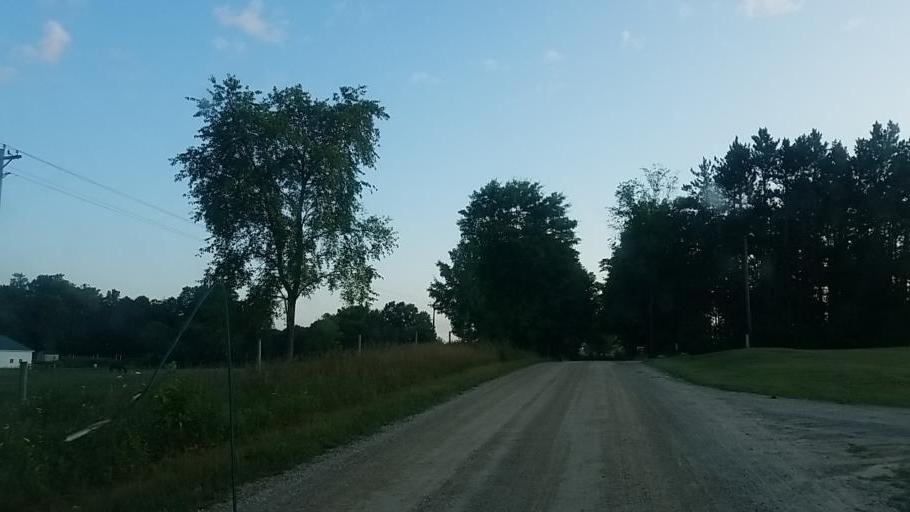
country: US
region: Michigan
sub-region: Osceola County
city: Evart
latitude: 43.9132
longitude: -85.2066
